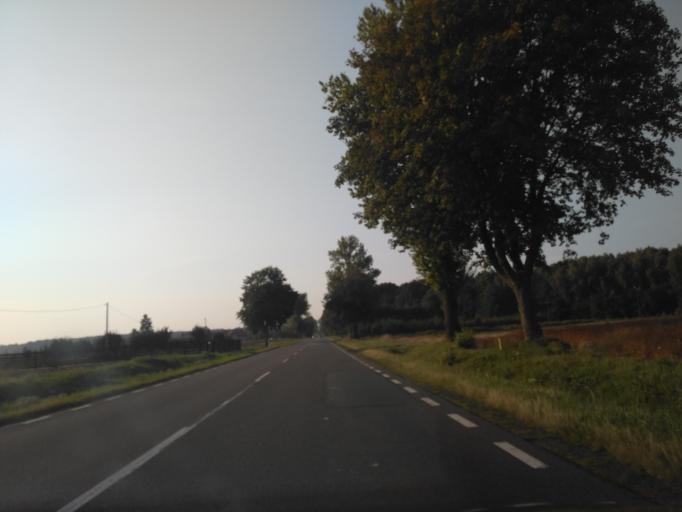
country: PL
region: Lublin Voivodeship
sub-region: Powiat krasnicki
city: Krasnik
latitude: 50.8752
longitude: 22.2671
